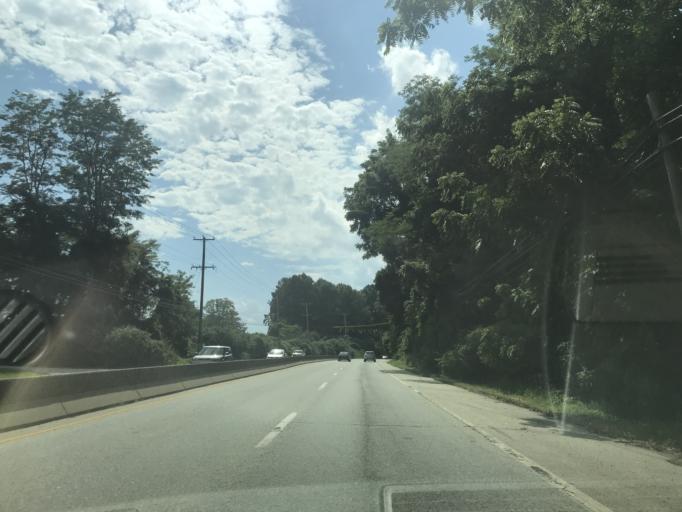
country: US
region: Pennsylvania
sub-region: Chester County
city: Kennett Square
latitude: 39.8737
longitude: -75.6276
